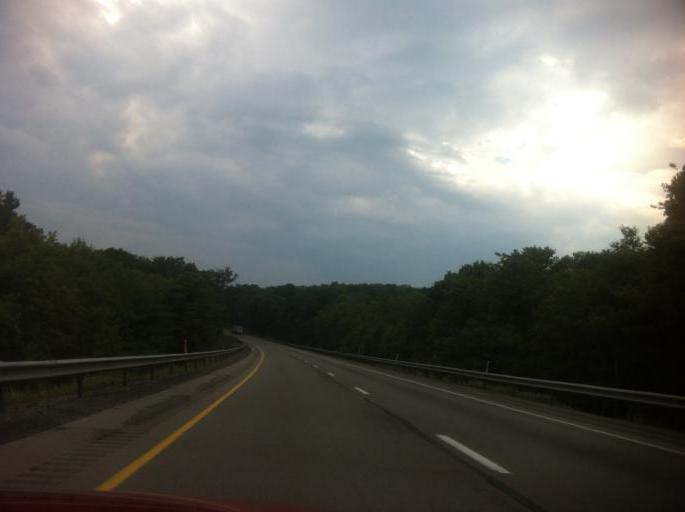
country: US
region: Pennsylvania
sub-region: Jefferson County
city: Brookville
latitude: 41.1790
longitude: -79.1240
